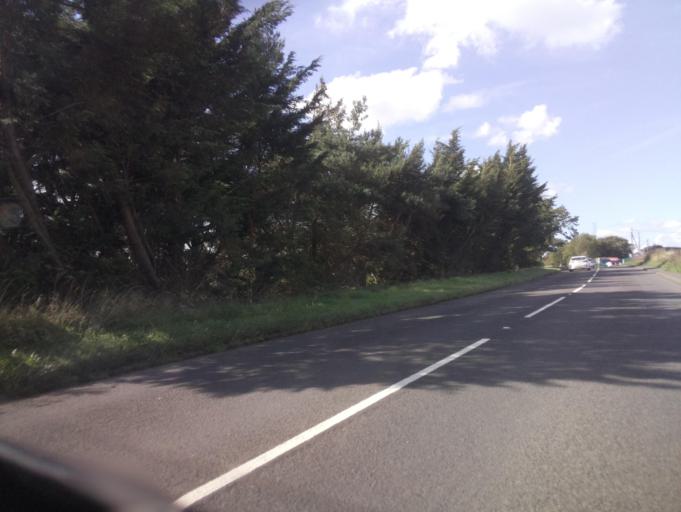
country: GB
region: Scotland
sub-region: Stirling
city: Bannockburn
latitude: 56.0796
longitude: -3.8960
